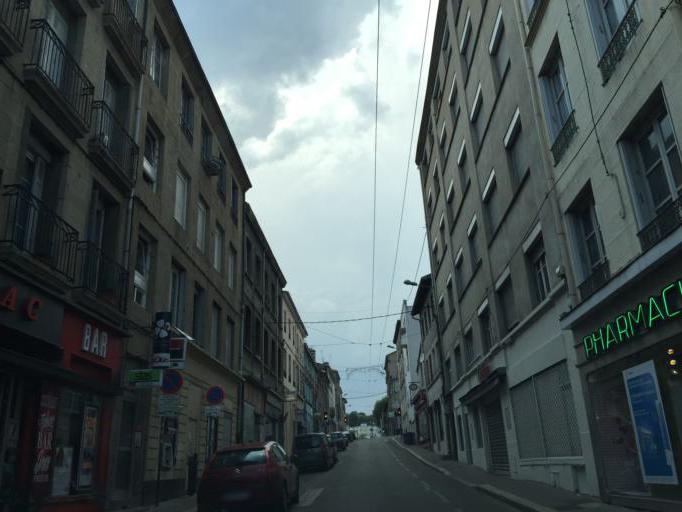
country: FR
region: Rhone-Alpes
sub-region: Departement de la Loire
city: Saint-Etienne
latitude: 45.4274
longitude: 4.3862
